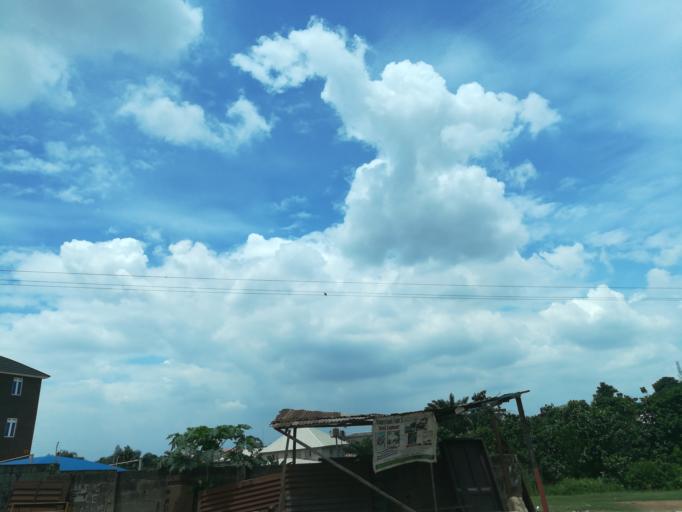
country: NG
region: Lagos
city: Ebute Ikorodu
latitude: 6.5983
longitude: 3.4968
